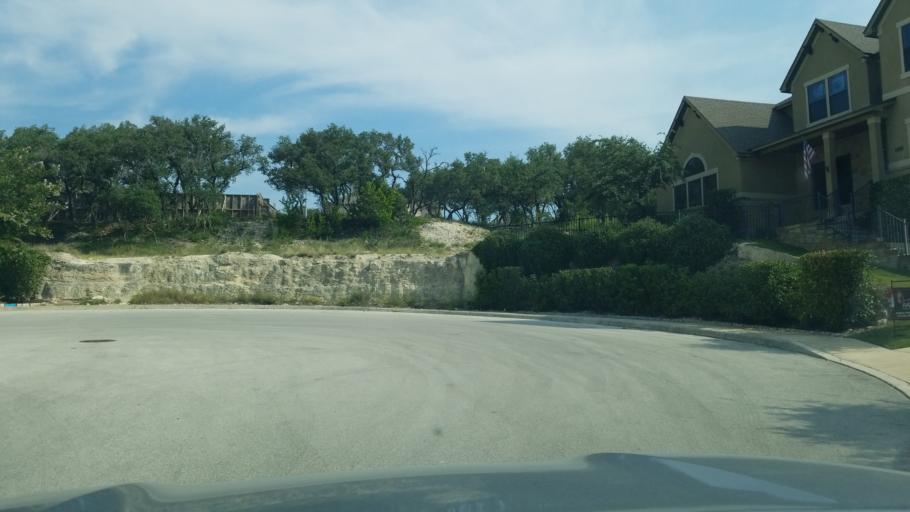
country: US
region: Texas
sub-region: Bexar County
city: Scenic Oaks
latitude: 29.7167
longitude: -98.6563
